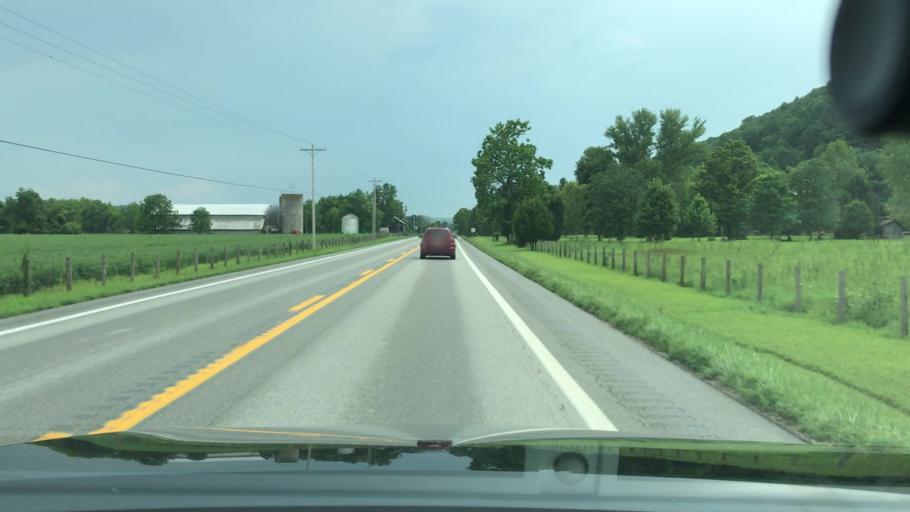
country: US
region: West Virginia
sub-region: Putnam County
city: Buffalo
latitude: 38.6588
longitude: -81.9690
